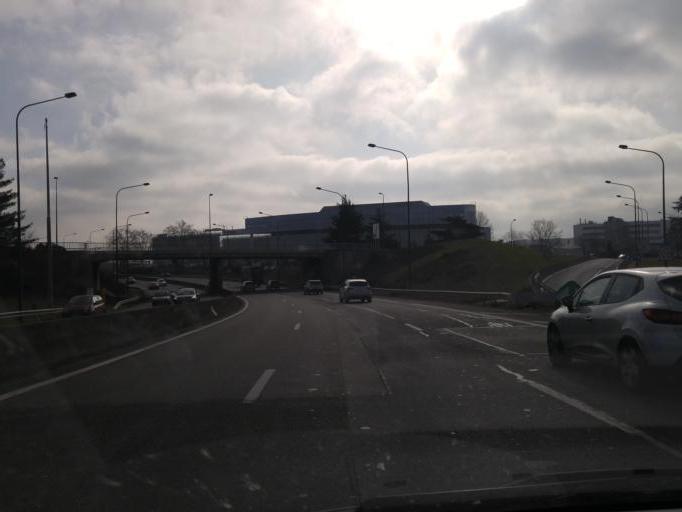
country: FR
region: Midi-Pyrenees
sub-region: Departement de la Haute-Garonne
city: Blagnac
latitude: 43.6273
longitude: 1.3839
